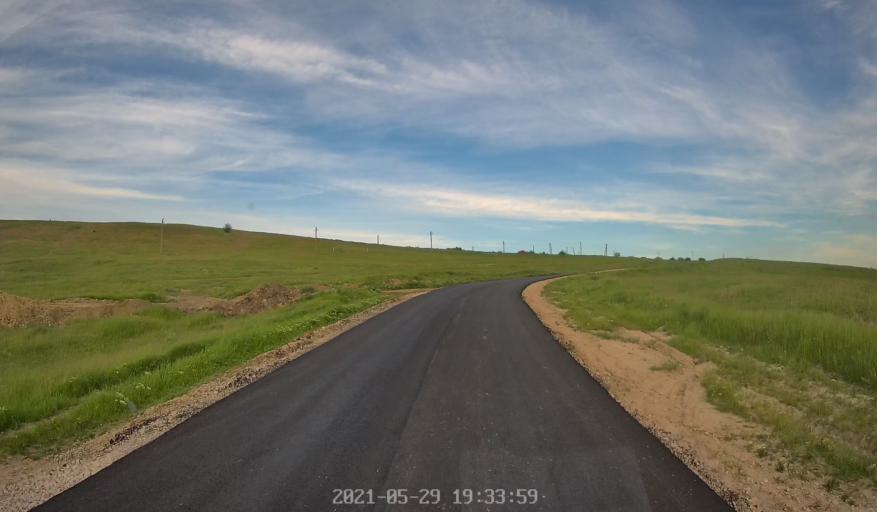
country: MD
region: Chisinau
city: Singera
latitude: 46.8288
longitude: 28.9581
